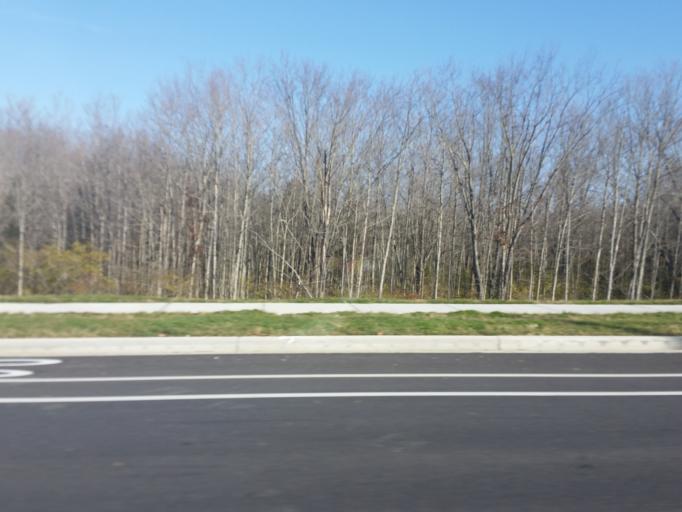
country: US
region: Ohio
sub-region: Butler County
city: Oxford
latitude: 39.4966
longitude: -84.7277
